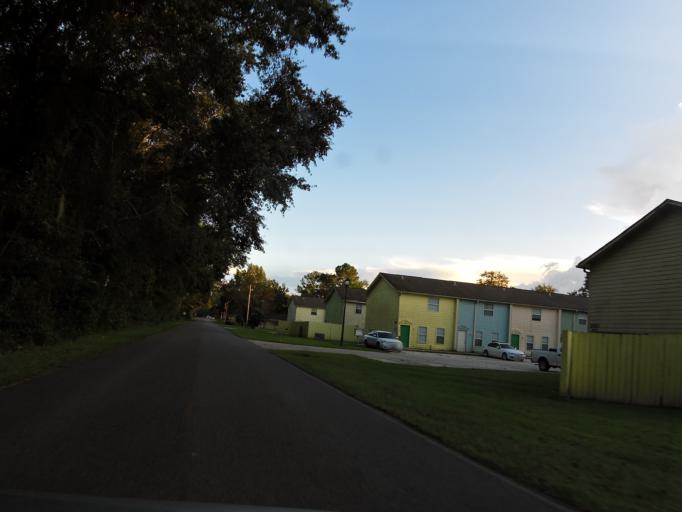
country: US
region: Georgia
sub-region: Camden County
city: Kingsland
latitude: 30.7968
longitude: -81.6910
